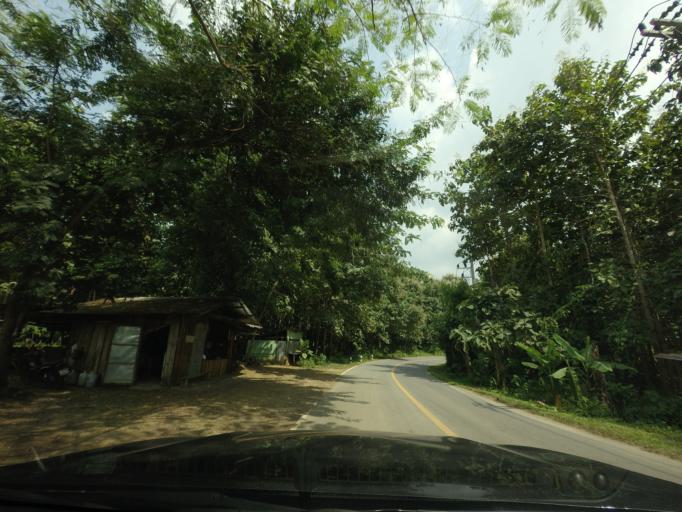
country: TH
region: Nan
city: Pua
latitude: 19.1792
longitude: 100.9465
